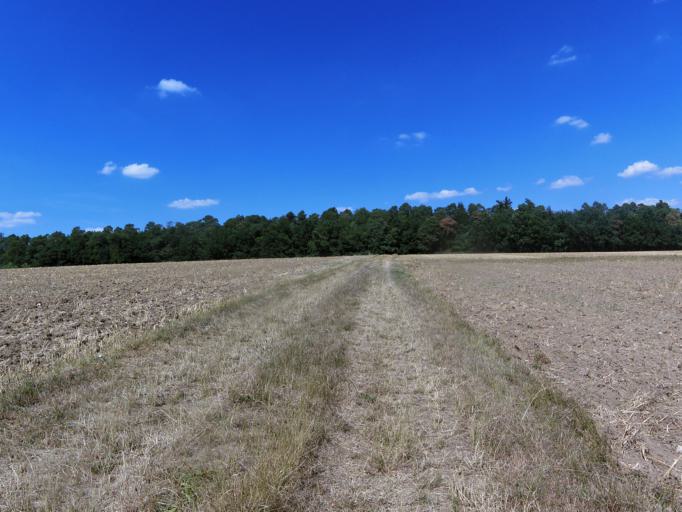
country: DE
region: Bavaria
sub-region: Regierungsbezirk Unterfranken
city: Gadheim
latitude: 49.8310
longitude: 9.9119
